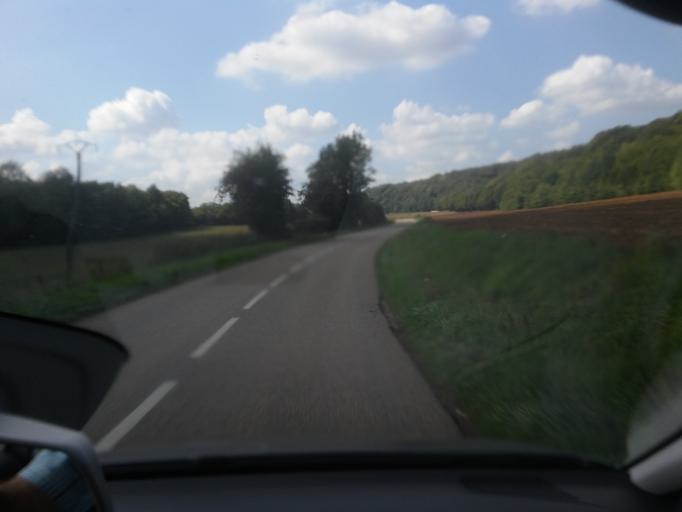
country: BE
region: Wallonia
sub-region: Province du Luxembourg
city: Rouvroy
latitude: 49.4954
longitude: 5.5376
